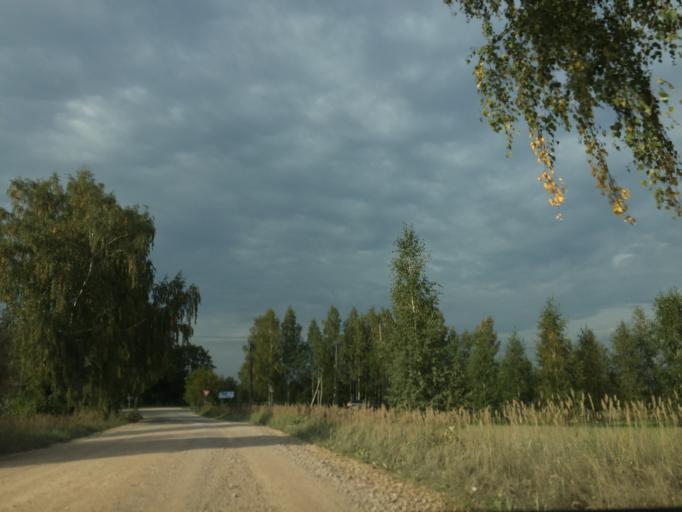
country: LV
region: Ikskile
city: Ikskile
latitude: 56.8193
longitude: 24.4488
